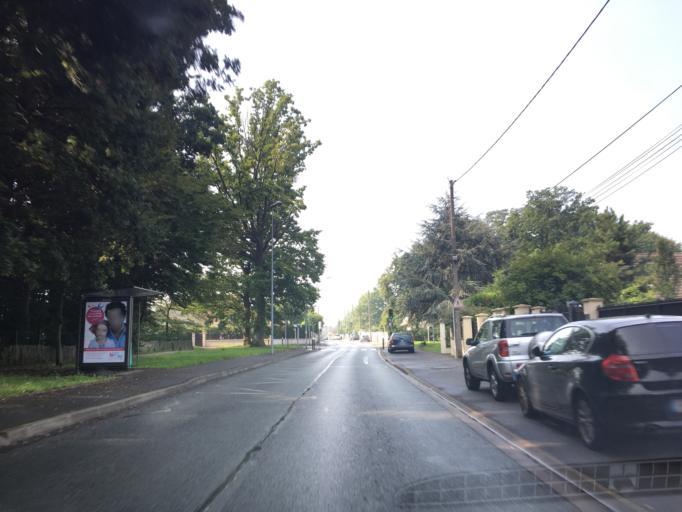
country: FR
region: Ile-de-France
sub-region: Departement du Val-de-Marne
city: Sucy-en-Brie
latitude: 48.7595
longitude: 2.5307
